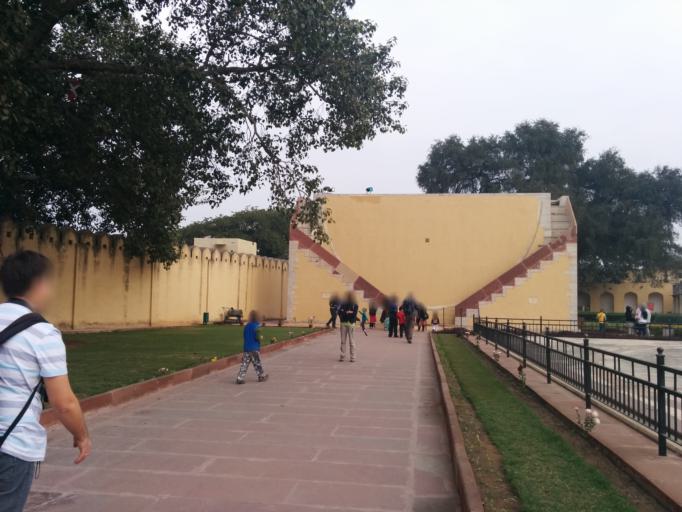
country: IN
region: Rajasthan
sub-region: Jaipur
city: Jaipur
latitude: 26.9252
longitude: 75.8245
